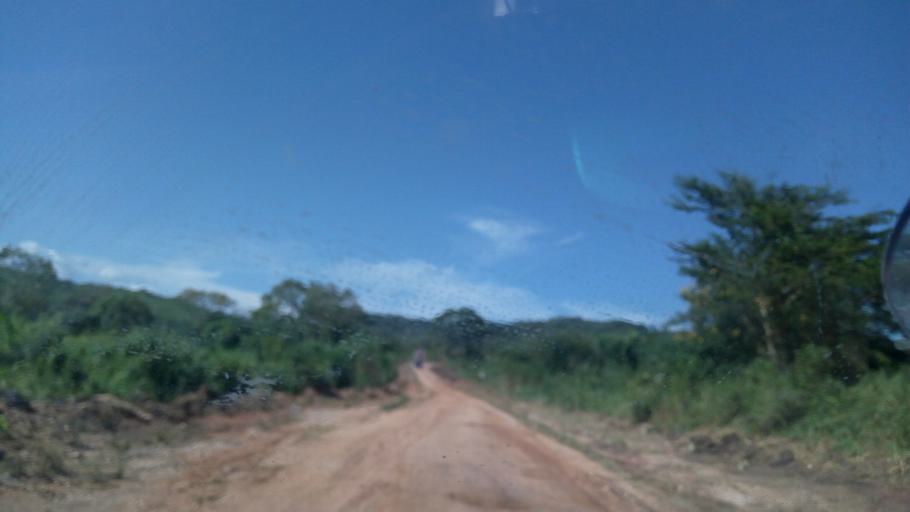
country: BI
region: Bururi
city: Rumonge
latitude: -4.4990
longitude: 28.8277
